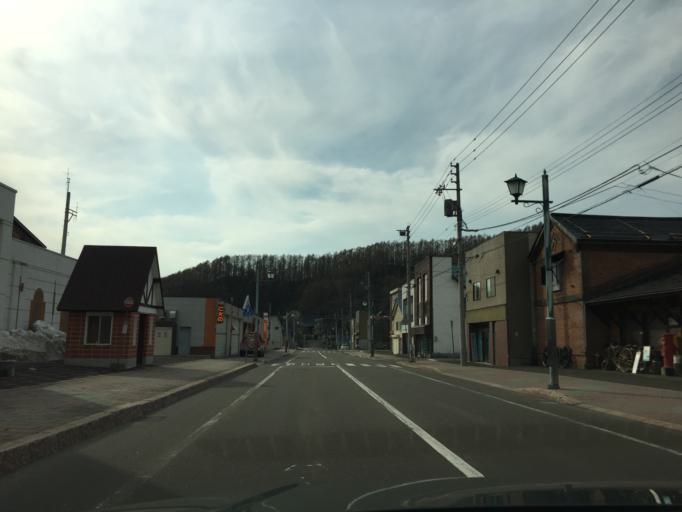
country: JP
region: Hokkaido
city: Utashinai
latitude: 43.5216
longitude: 142.0420
